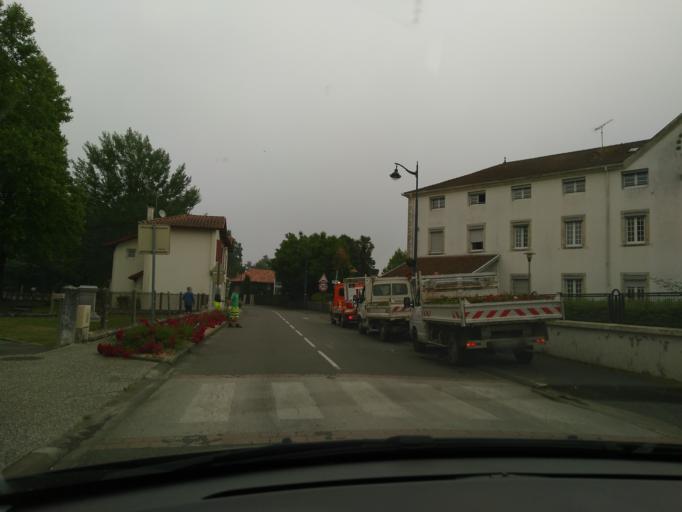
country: FR
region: Aquitaine
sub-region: Departement des Landes
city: Saint-Vincent-de-Paul
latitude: 43.7840
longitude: -0.9904
